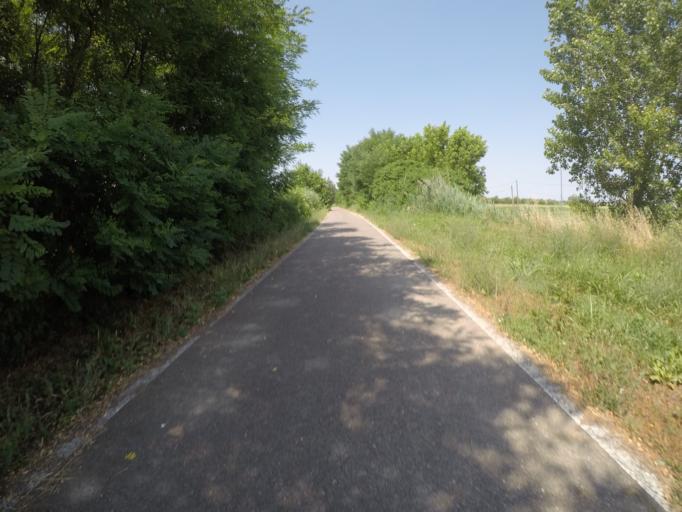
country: IT
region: Veneto
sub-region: Provincia di Rovigo
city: Villamarzana
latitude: 45.0090
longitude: 11.6727
